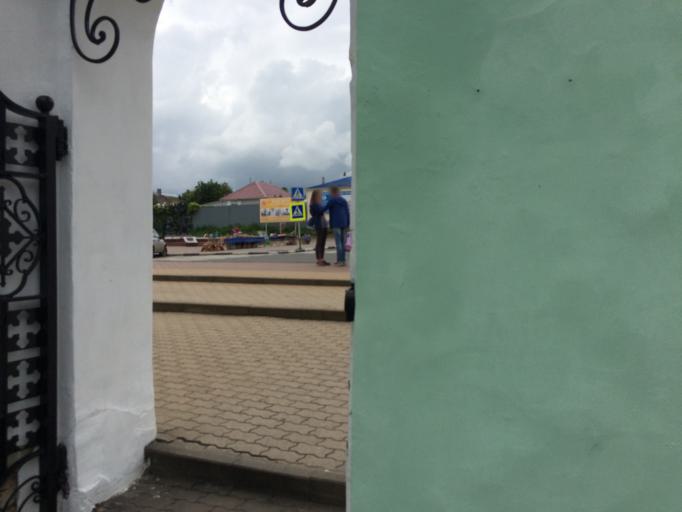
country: RU
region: Kursk
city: Zolotukhino
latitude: 51.9733
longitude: 36.3110
